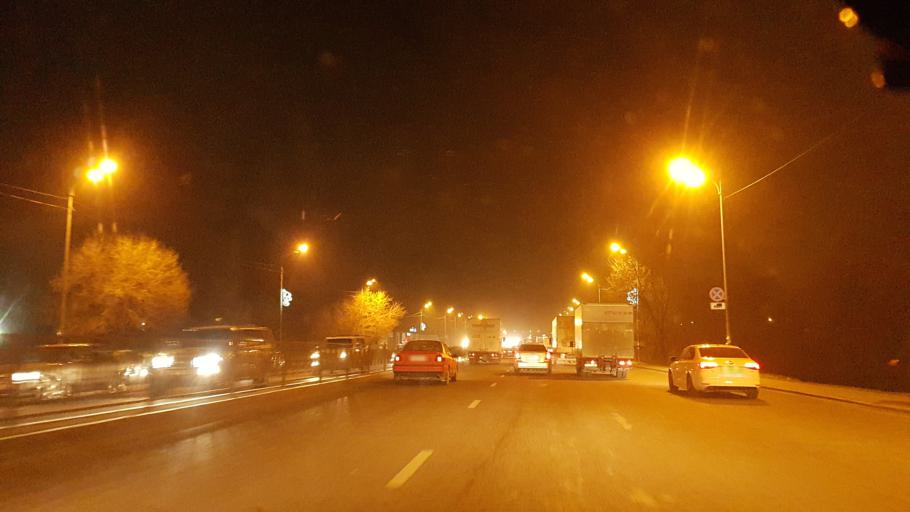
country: KZ
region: Almaty Qalasy
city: Almaty
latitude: 43.2653
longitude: 76.8662
